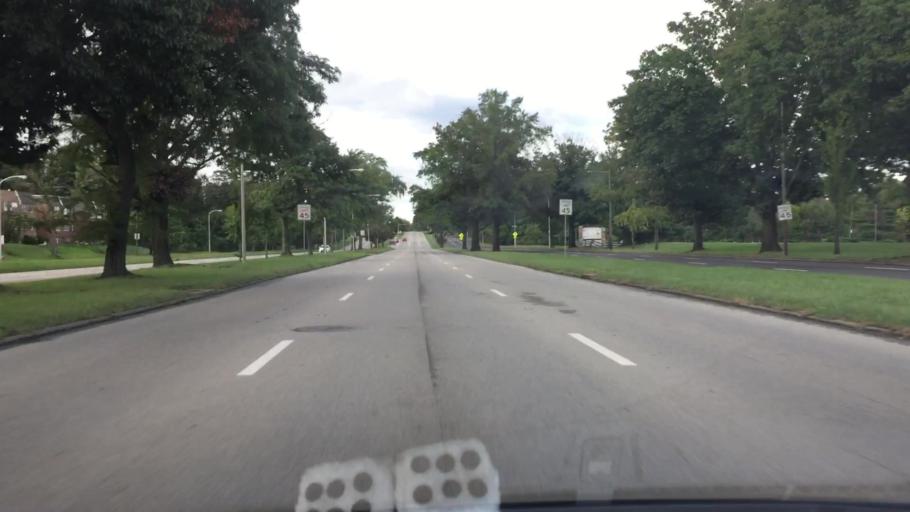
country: US
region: Pennsylvania
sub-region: Bucks County
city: Feasterville
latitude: 40.0860
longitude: -75.0235
